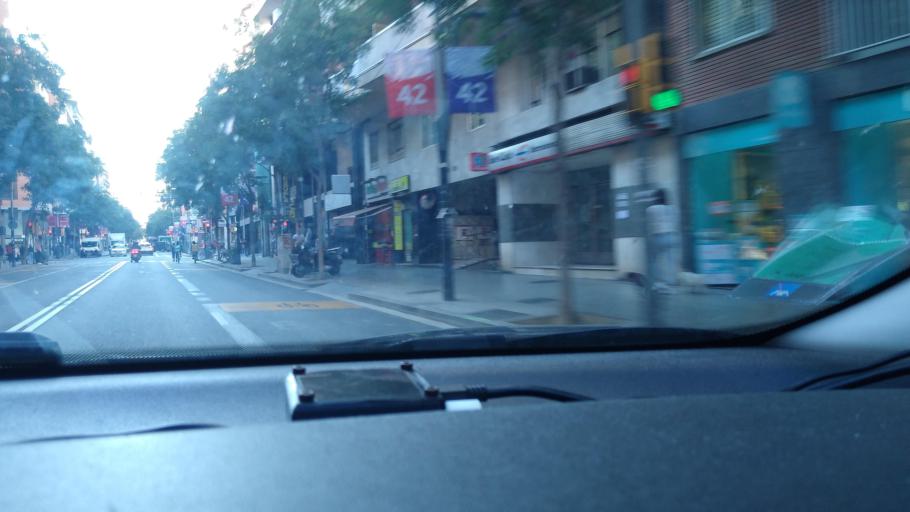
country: ES
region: Catalonia
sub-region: Provincia de Barcelona
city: les Corts
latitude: 41.3754
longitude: 2.1282
